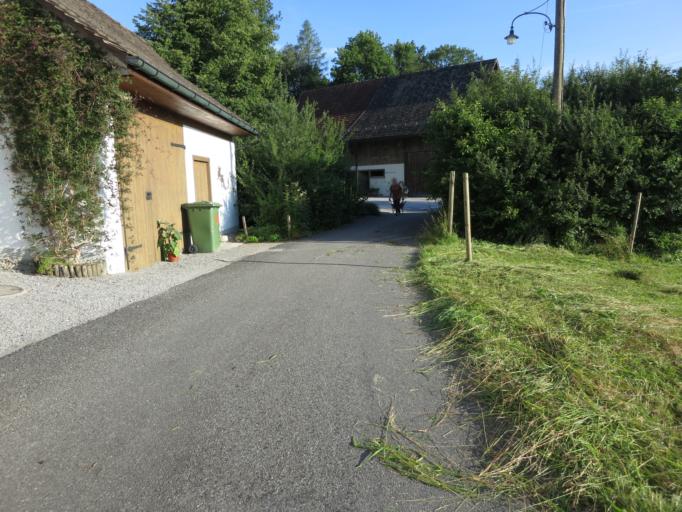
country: CH
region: Zurich
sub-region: Bezirk Hinwil
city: Bubikon
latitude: 47.2543
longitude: 8.8156
